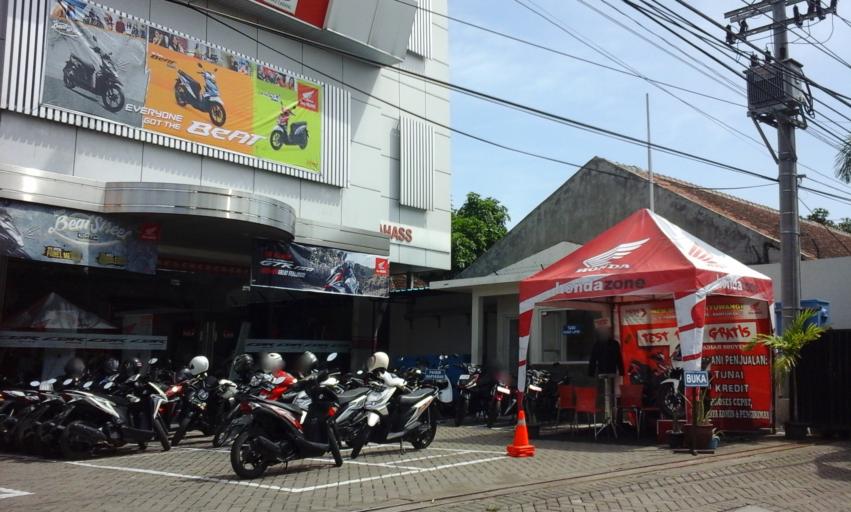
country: ID
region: East Java
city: Krajan
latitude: -8.2396
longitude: 114.3558
